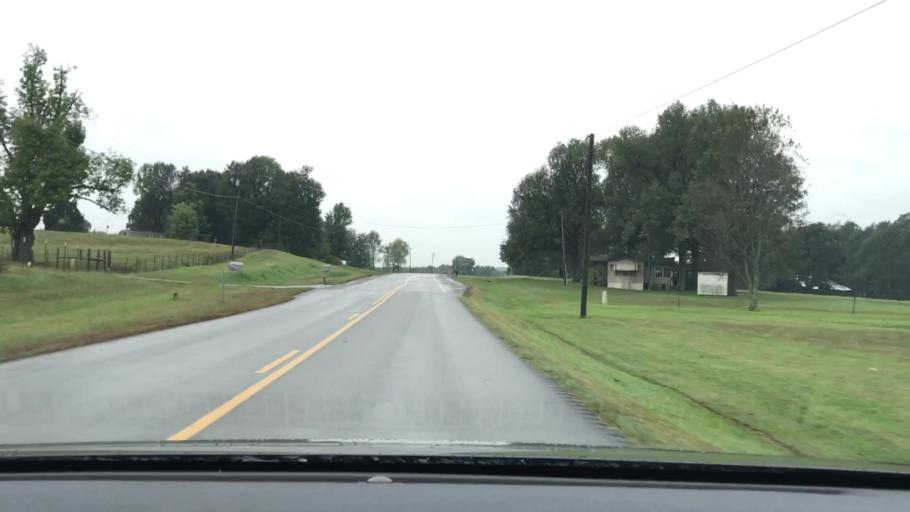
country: US
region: Kentucky
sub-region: Hopkins County
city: Madisonville
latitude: 37.3382
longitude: -87.4137
